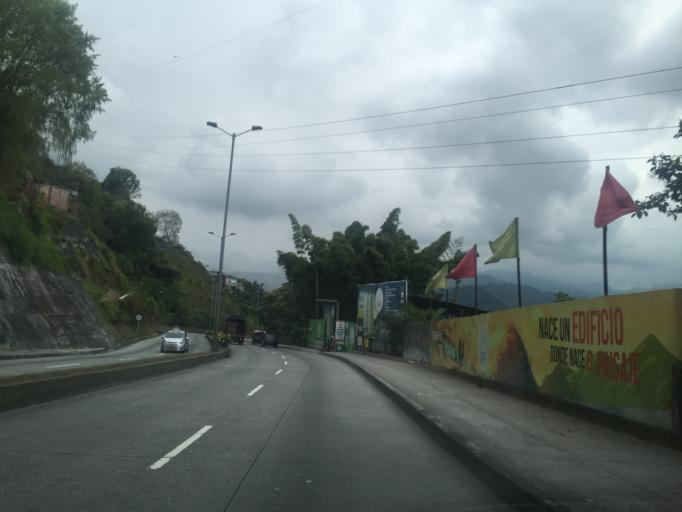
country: CO
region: Caldas
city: Villamaria
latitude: 5.0458
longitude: -75.4838
